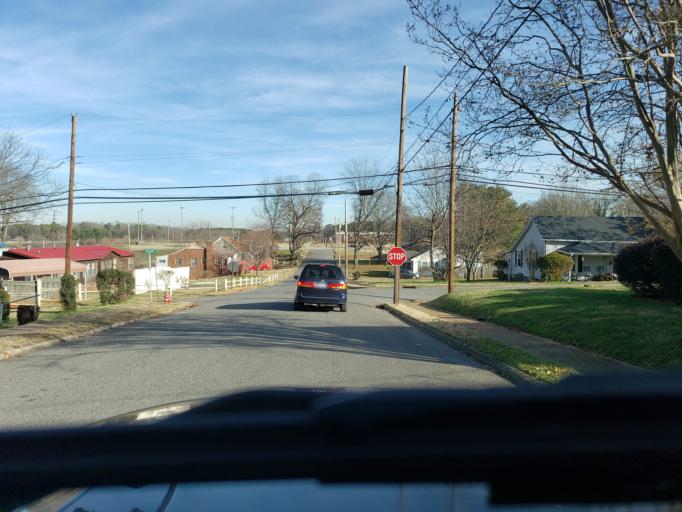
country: US
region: North Carolina
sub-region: Cleveland County
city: Kings Mountain
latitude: 35.2441
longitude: -81.3367
